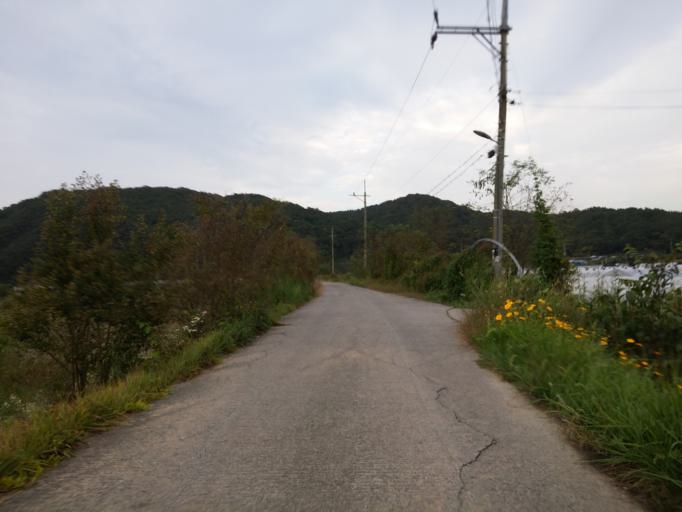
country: KR
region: Daejeon
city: Daejeon
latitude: 36.2520
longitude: 127.3229
